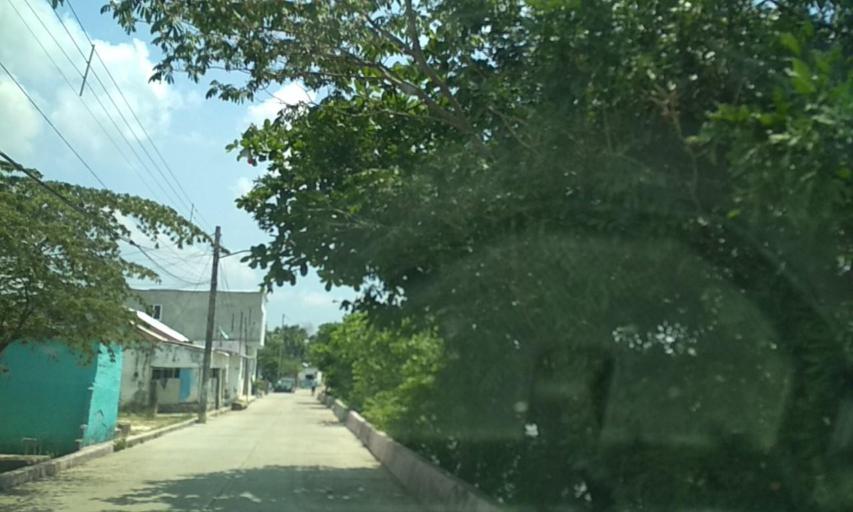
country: MX
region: Veracruz
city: Las Choapas
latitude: 17.9116
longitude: -94.0873
